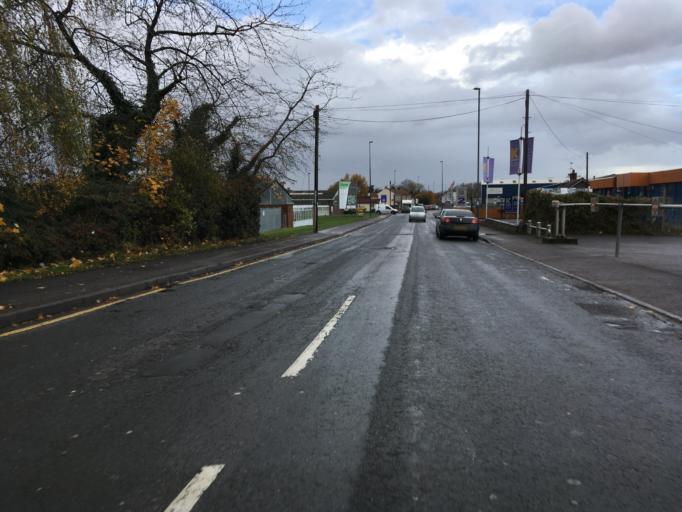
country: GB
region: England
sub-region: South Gloucestershire
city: Yate
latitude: 51.5420
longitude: -2.4329
